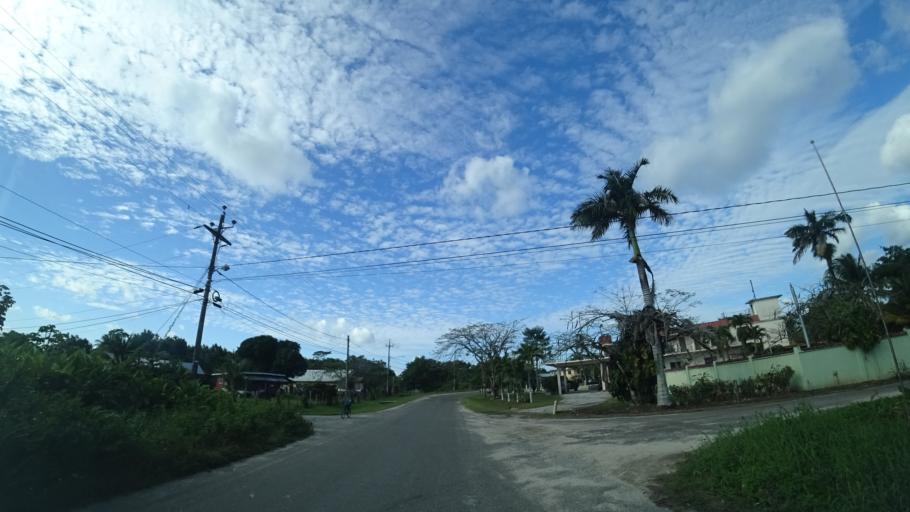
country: BZ
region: Belize
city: Belize City
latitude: 17.5654
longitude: -88.4065
